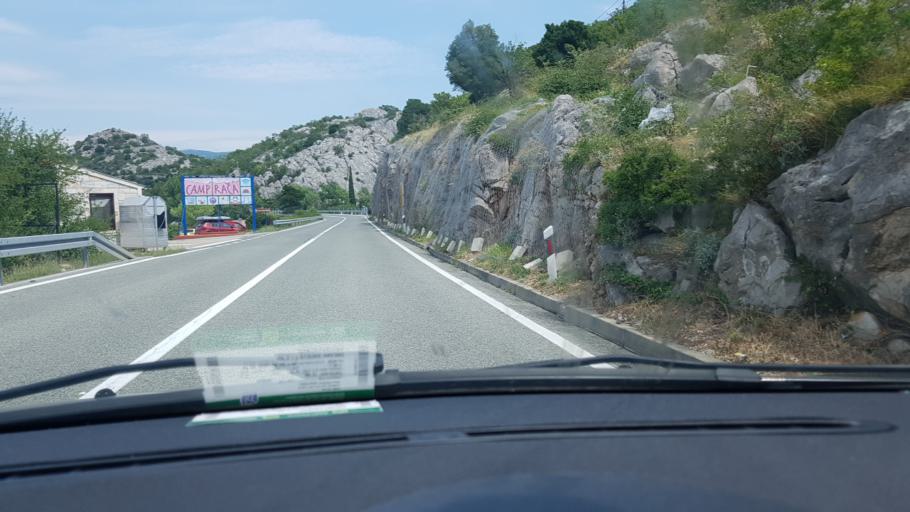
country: HR
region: Licko-Senjska
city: Senj
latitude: 44.9153
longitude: 14.9138
